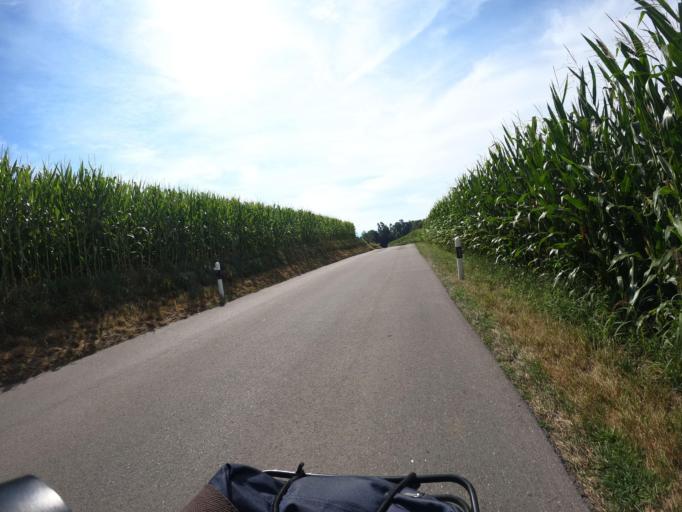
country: CH
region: Zurich
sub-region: Bezirk Affoltern
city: Hedingen
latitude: 47.3104
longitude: 8.4262
